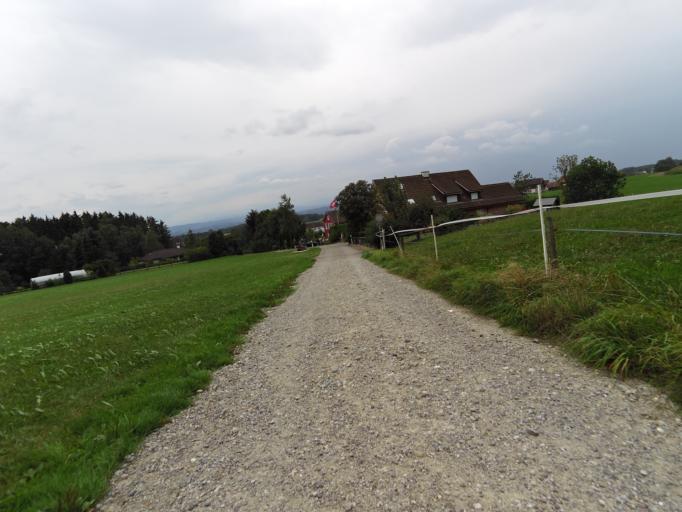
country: CH
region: Thurgau
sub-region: Kreuzlingen District
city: Ermatingen
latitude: 47.6408
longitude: 9.0555
